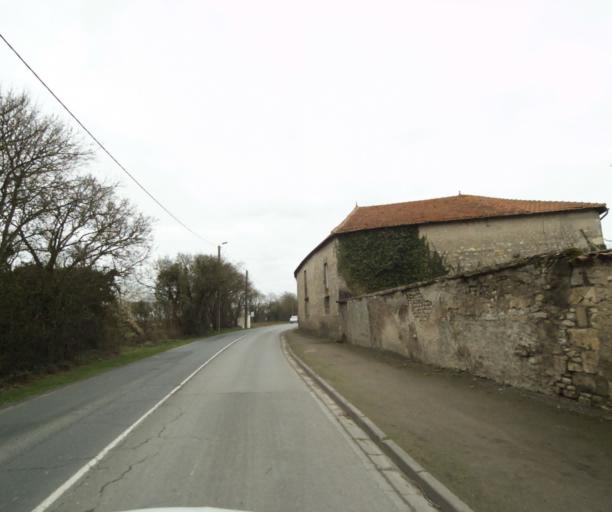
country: FR
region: Poitou-Charentes
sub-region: Departement de la Charente-Maritime
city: Nieul-sur-Mer
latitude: 46.1979
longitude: -1.1582
